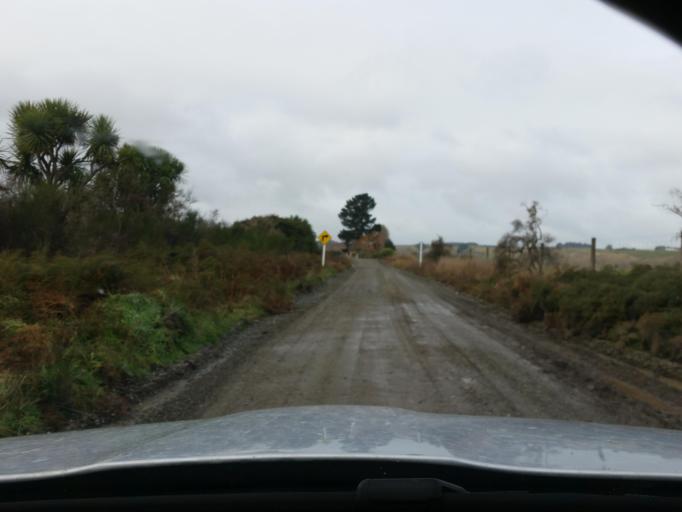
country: NZ
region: Southland
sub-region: Southland District
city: Riverton
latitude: -45.9370
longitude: 167.7045
